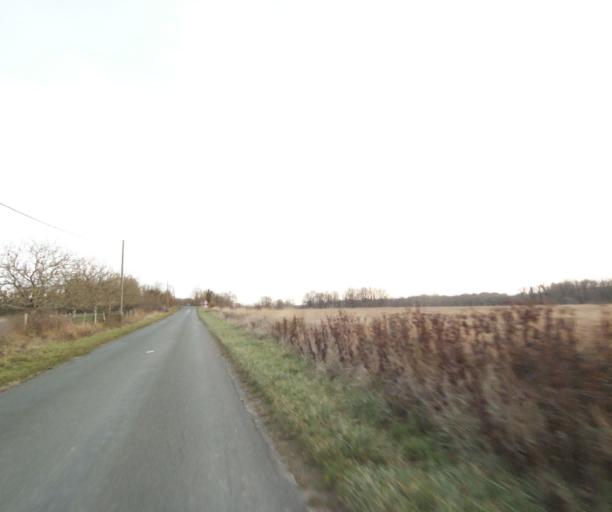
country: FR
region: Poitou-Charentes
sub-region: Departement de la Charente-Maritime
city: Fontcouverte
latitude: 45.8013
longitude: -0.5772
